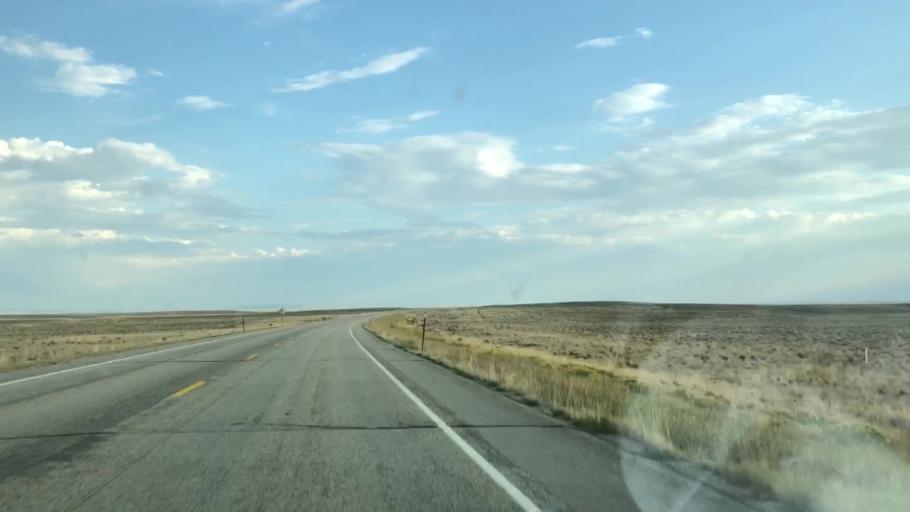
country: US
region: Wyoming
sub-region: Sweetwater County
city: North Rock Springs
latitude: 42.2567
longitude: -109.4694
